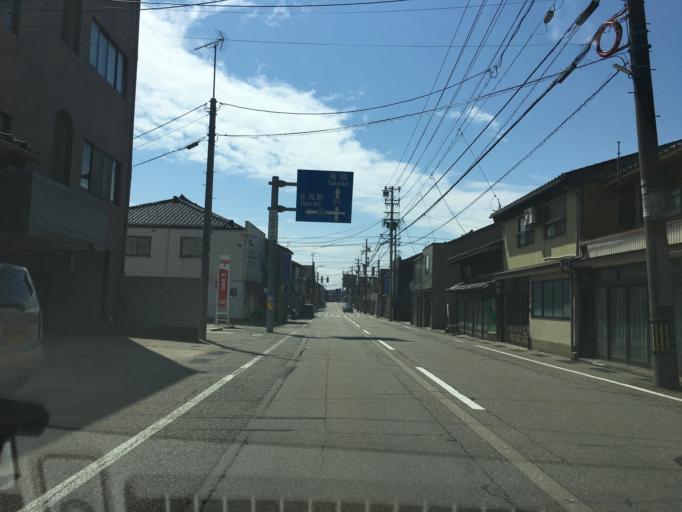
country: JP
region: Toyama
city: Himi
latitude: 36.8496
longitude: 136.9877
